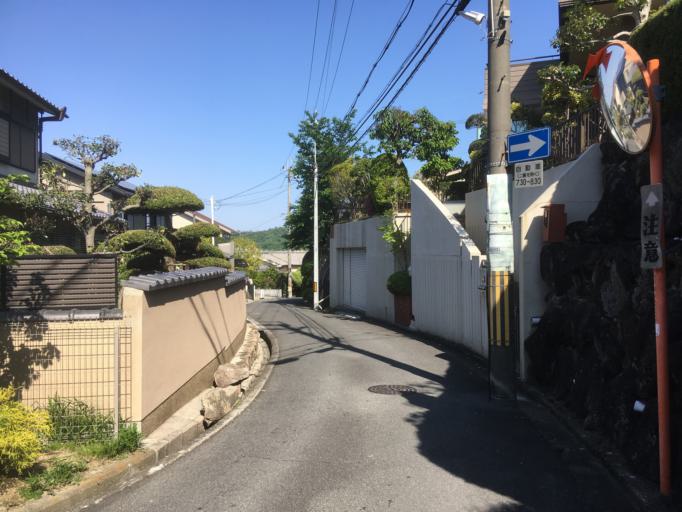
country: JP
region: Nara
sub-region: Ikoma-shi
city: Ikoma
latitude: 34.6899
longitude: 135.6998
